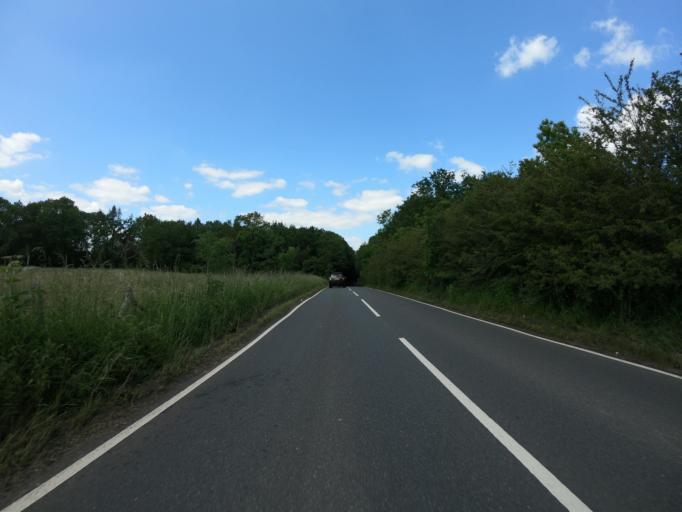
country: GB
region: England
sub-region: Kent
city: Halstead
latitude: 51.3120
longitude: 0.1356
